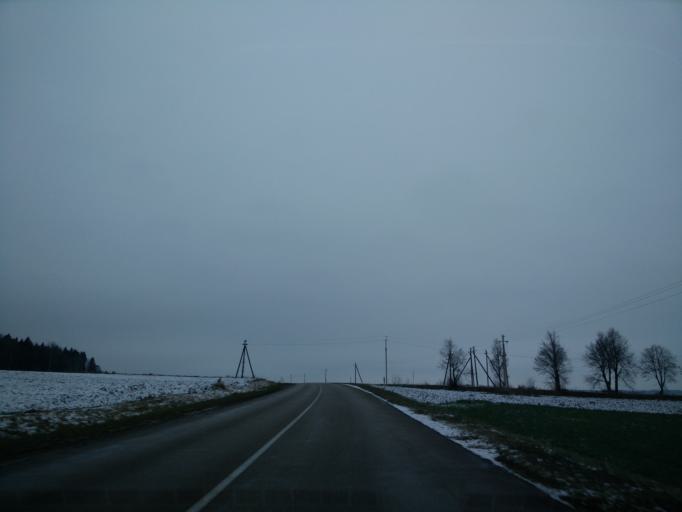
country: LT
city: Ariogala
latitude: 55.3476
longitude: 23.3897
